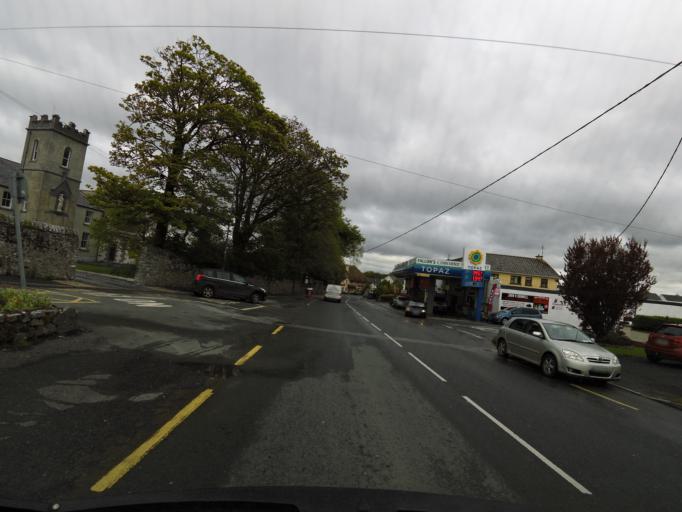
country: IE
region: Connaught
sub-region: County Galway
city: Oranmore
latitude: 53.1391
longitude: -8.9420
